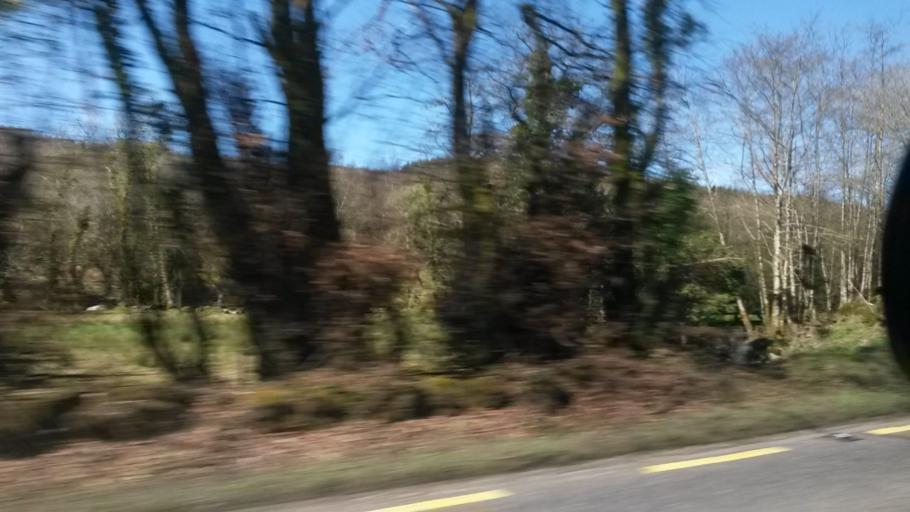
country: IE
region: Munster
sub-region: County Cork
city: Millstreet
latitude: 51.9529
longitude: -9.1846
